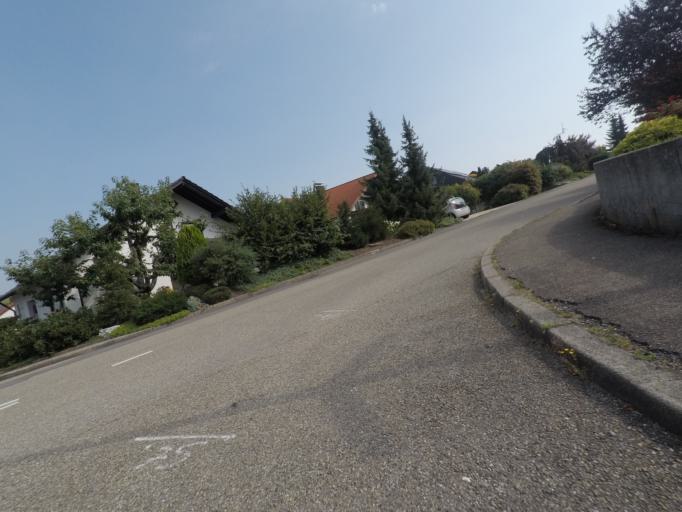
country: DE
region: Baden-Wuerttemberg
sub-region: Regierungsbezirk Stuttgart
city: Winterbach
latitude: 48.7935
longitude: 9.4861
